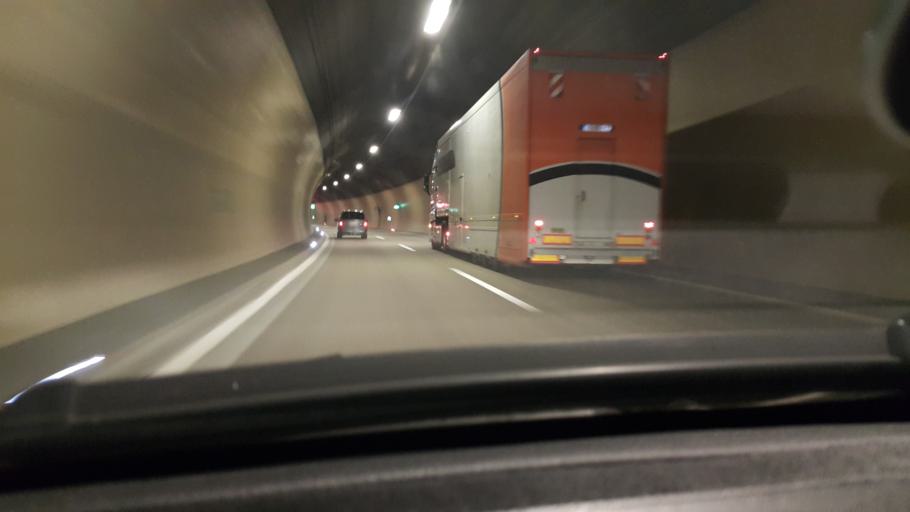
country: AT
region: Carinthia
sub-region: Klagenfurt am Woerthersee
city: Klagenfurt am Woerthersee
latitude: 46.6578
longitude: 14.2922
